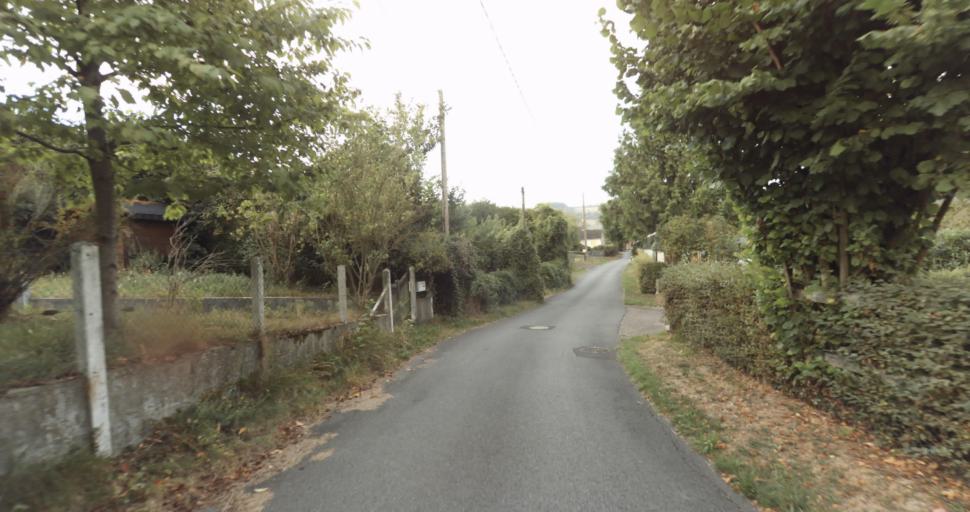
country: FR
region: Lower Normandy
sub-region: Departement de l'Orne
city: Vimoutiers
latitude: 48.9384
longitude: 0.2043
